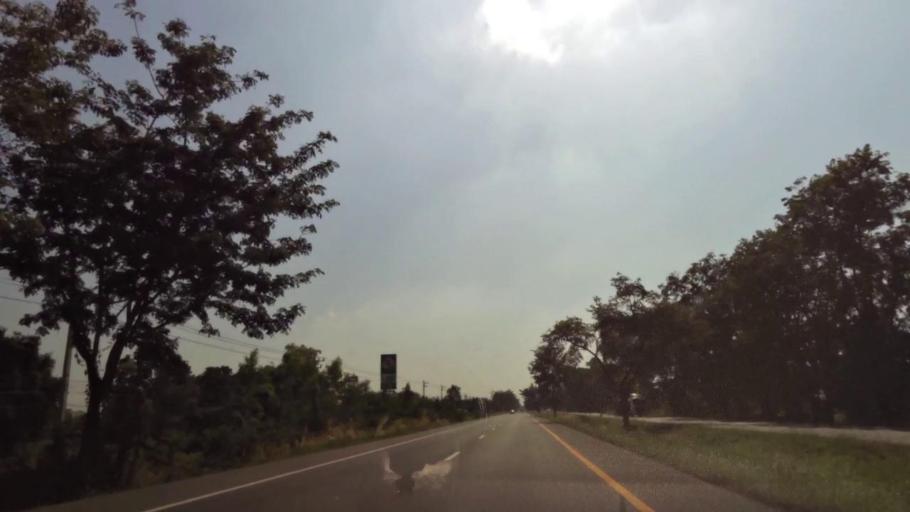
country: TH
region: Phichit
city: Bueng Na Rang
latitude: 16.2063
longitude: 100.1276
